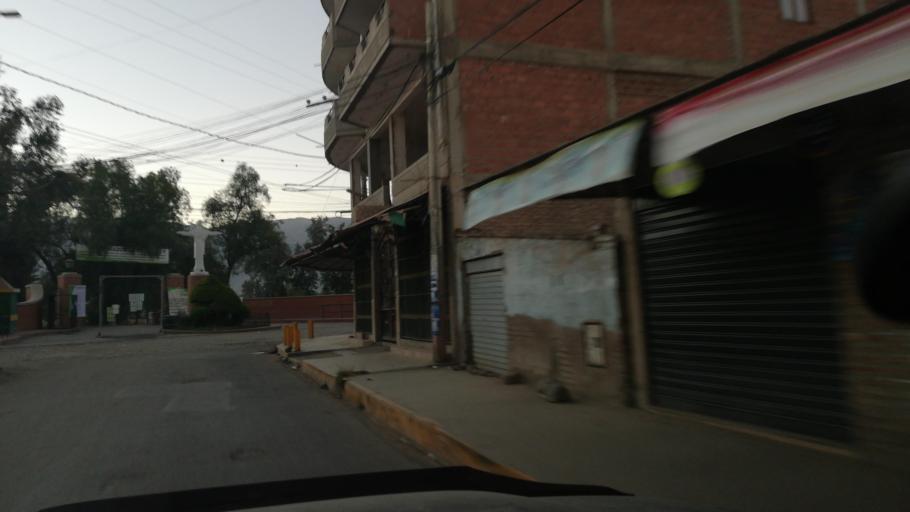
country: BO
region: Cochabamba
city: Cochabamba
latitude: -17.3815
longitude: -66.2214
